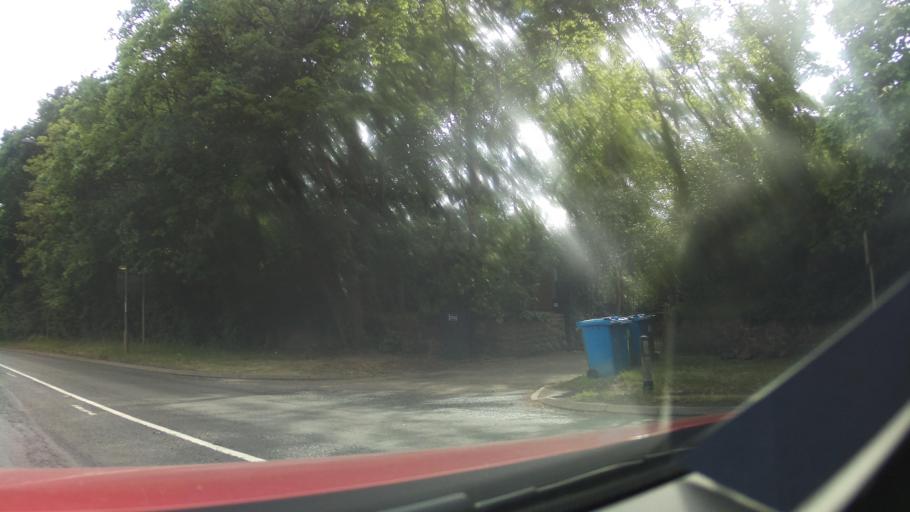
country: GB
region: England
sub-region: Dudley
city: Kingswinford
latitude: 52.5322
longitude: -2.1782
